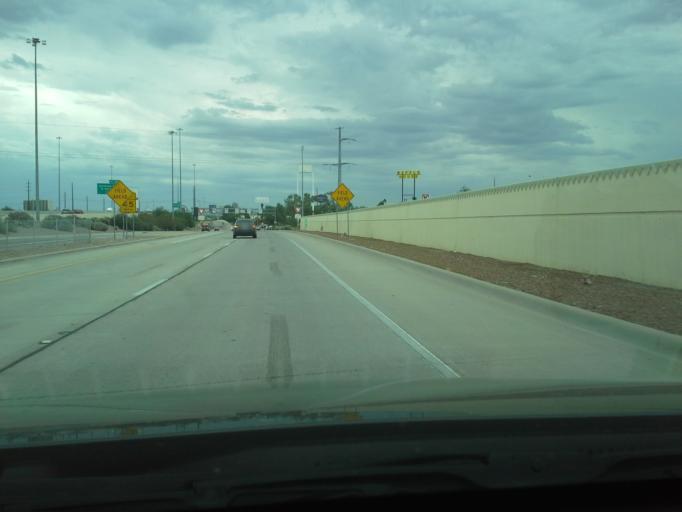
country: US
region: Arizona
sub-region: Pima County
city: Flowing Wells
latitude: 32.2531
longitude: -110.9957
